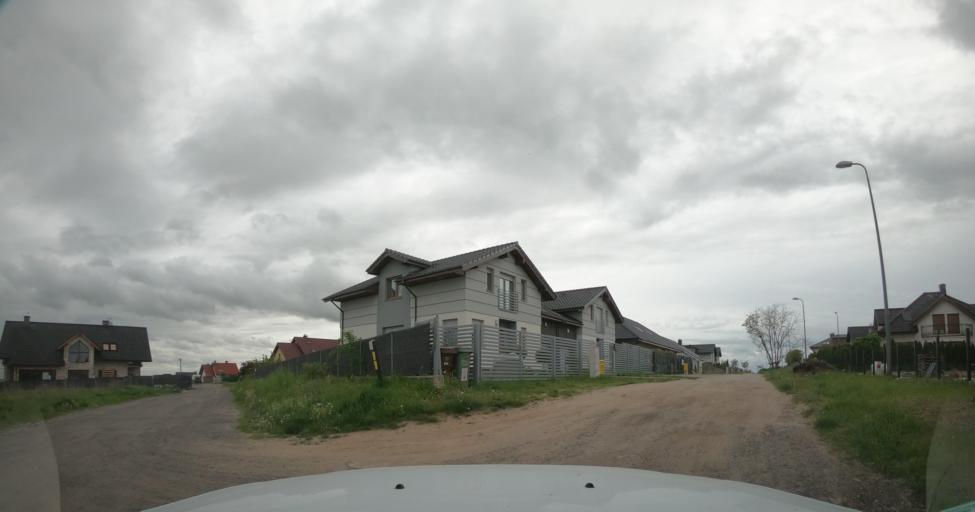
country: PL
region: West Pomeranian Voivodeship
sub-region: Powiat stargardzki
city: Stargard Szczecinski
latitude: 53.3149
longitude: 15.0479
